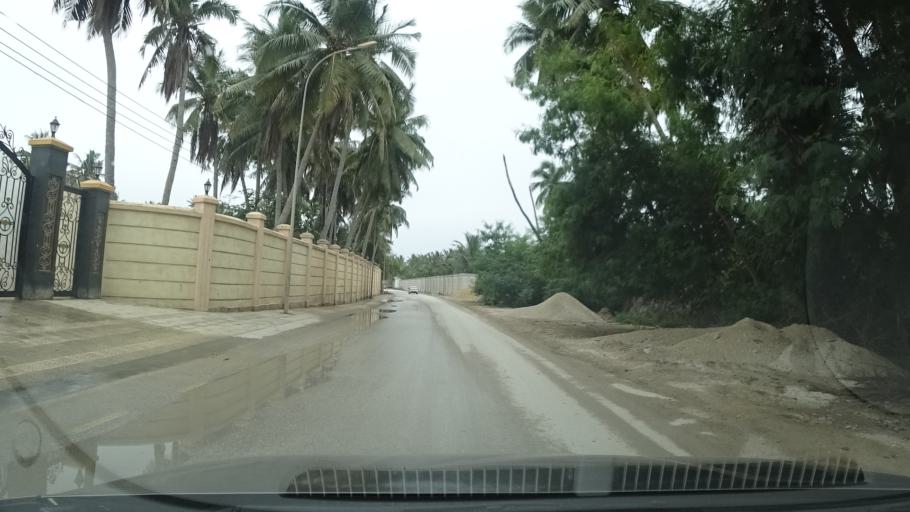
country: OM
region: Zufar
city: Salalah
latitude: 17.0079
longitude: 54.0981
